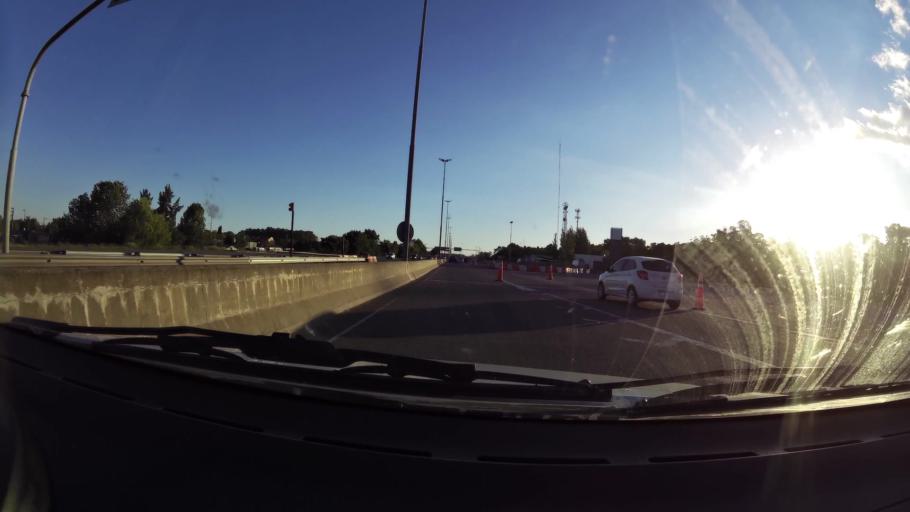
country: AR
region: Buenos Aires
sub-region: Partido de Quilmes
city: Quilmes
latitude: -34.7851
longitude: -58.1538
